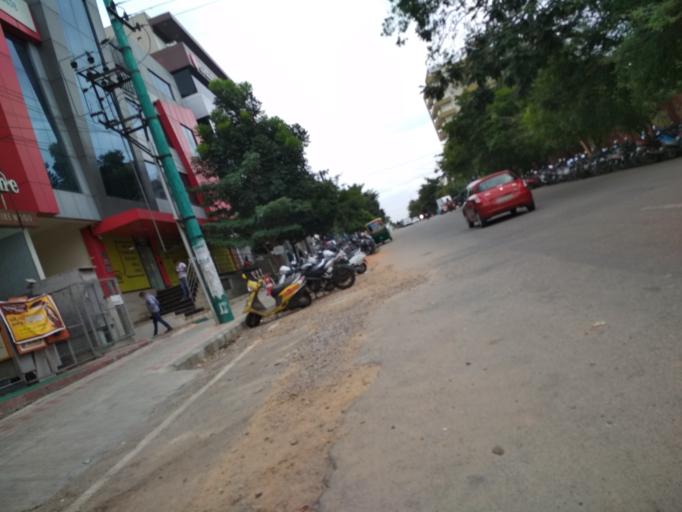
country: IN
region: Karnataka
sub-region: Bangalore Urban
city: Bangalore
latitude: 12.9204
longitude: 77.6451
